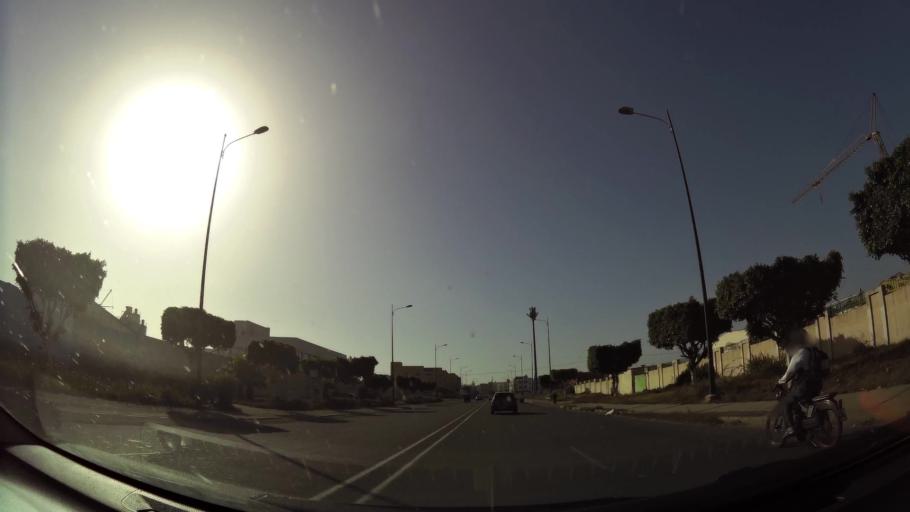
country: MA
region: Oued ed Dahab-Lagouira
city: Dakhla
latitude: 30.3920
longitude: -9.5309
